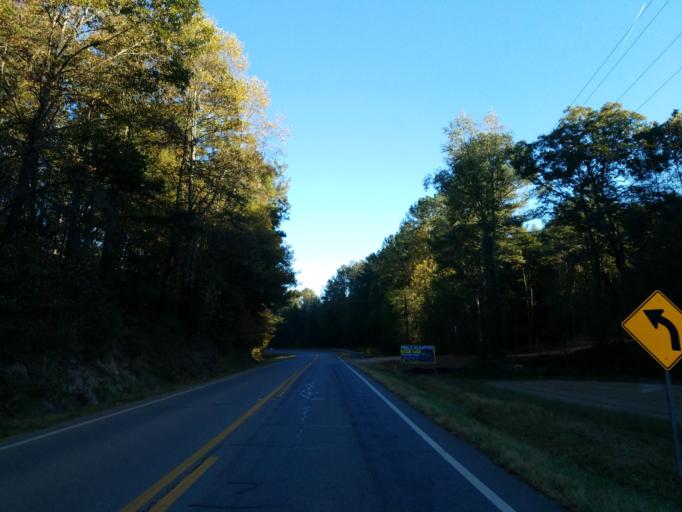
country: US
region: Georgia
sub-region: Dawson County
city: Dawsonville
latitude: 34.4250
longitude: -84.1530
